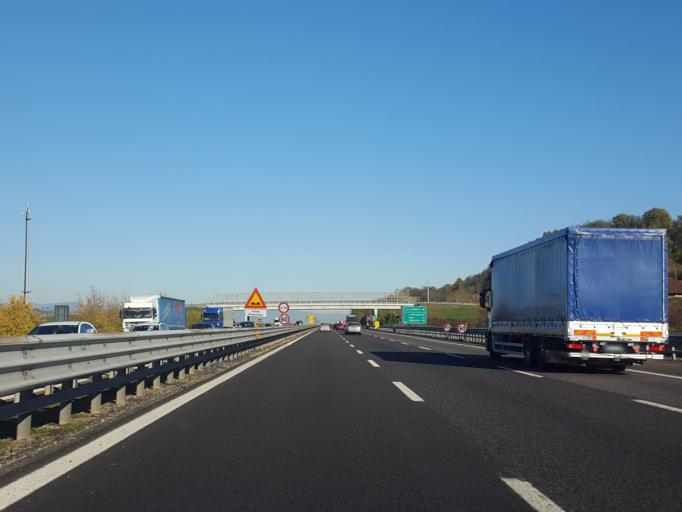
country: IT
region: Veneto
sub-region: Provincia di Vicenza
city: Brendola
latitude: 45.4950
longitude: 11.4474
